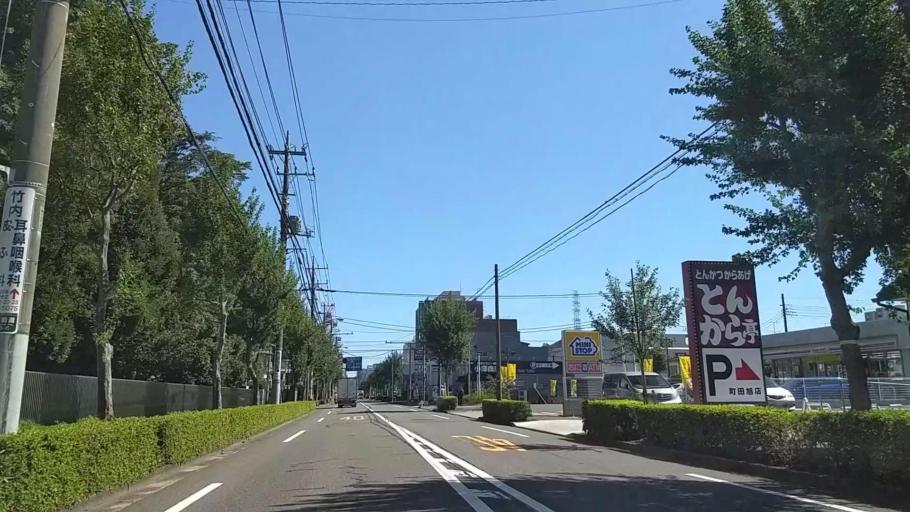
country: JP
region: Tokyo
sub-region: Machida-shi
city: Machida
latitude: 35.5566
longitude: 139.4403
